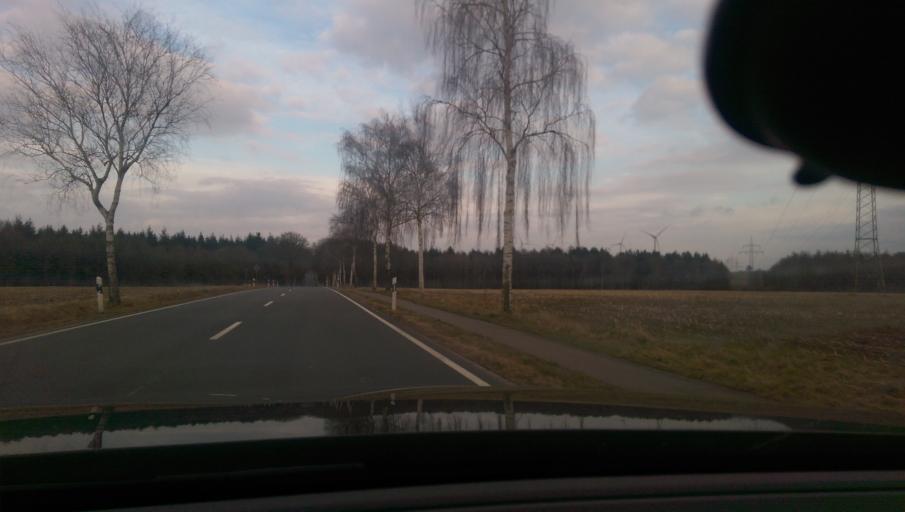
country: DE
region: Lower Saxony
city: Bohme
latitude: 52.8334
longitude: 9.4958
